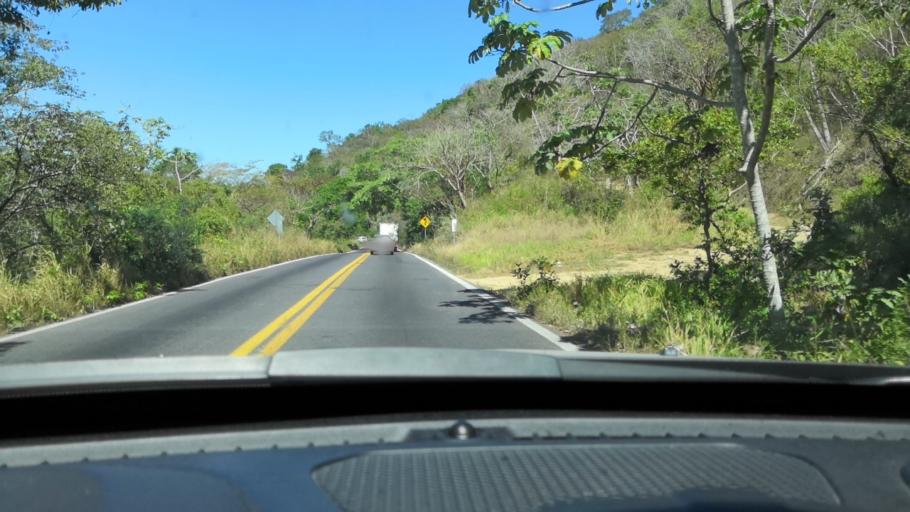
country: MX
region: Nayarit
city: Compostela
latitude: 21.2130
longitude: -104.9916
